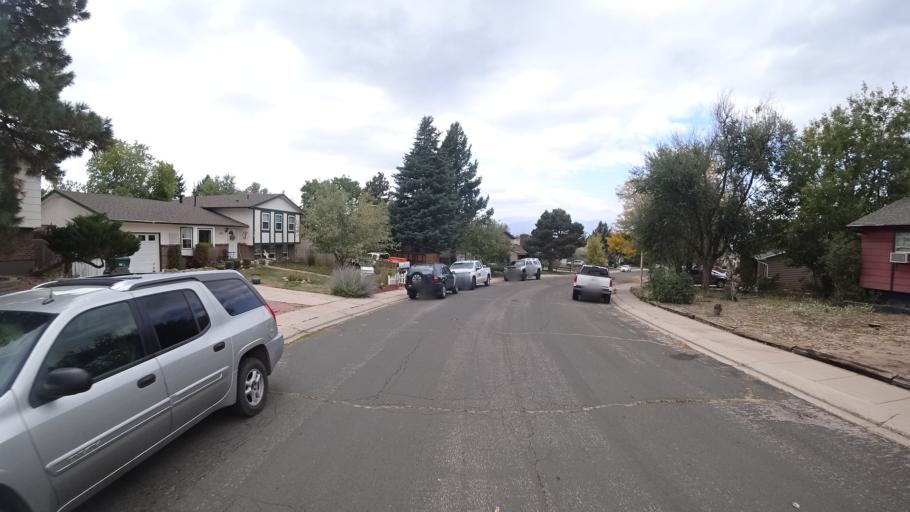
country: US
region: Colorado
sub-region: El Paso County
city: Cimarron Hills
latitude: 38.8897
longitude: -104.7362
